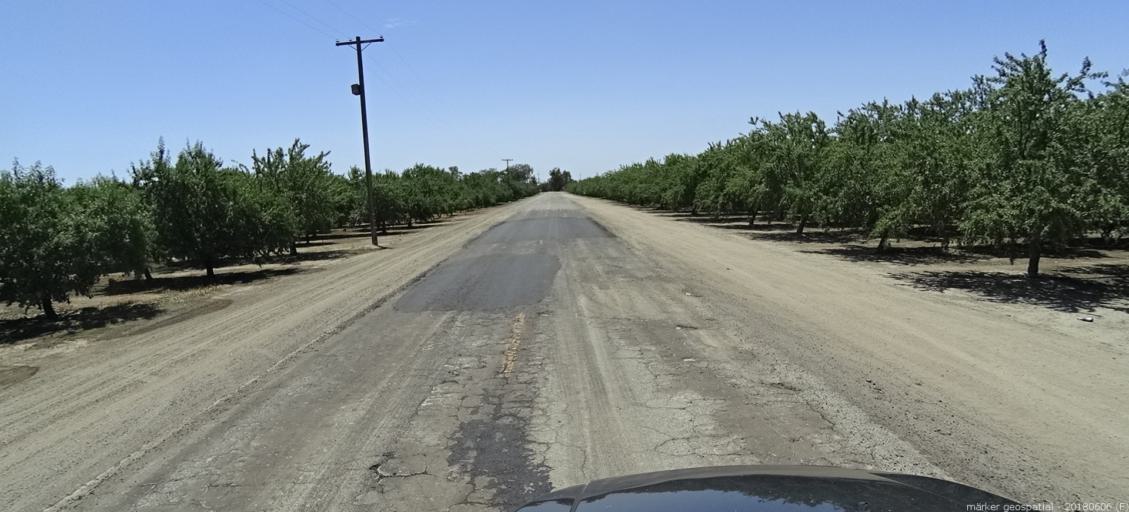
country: US
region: California
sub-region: Fresno County
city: Firebaugh
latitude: 36.8470
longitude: -120.4179
